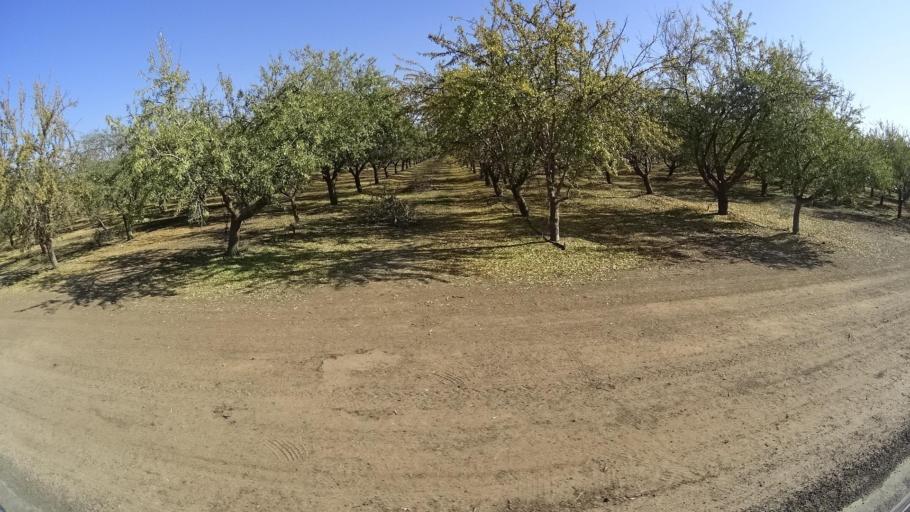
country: US
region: California
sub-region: Tulare County
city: Richgrove
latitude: 35.7352
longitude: -119.1341
